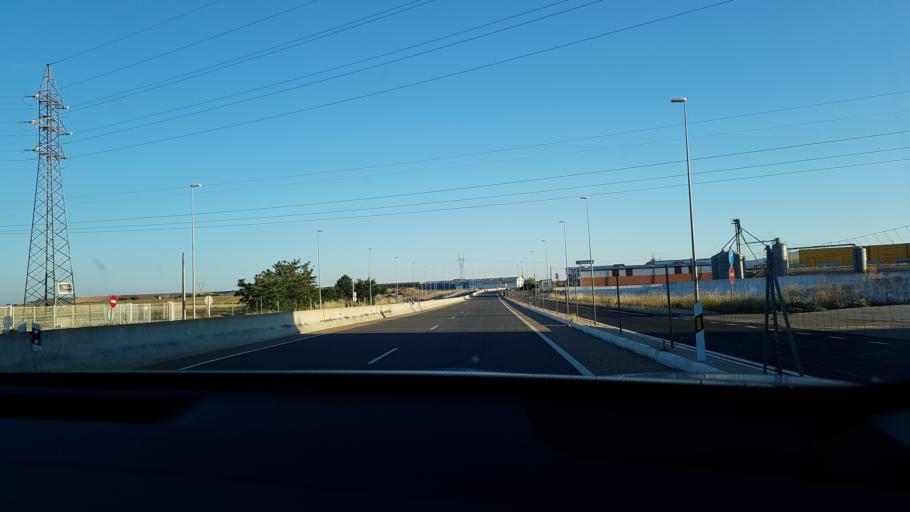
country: ES
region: Castille and Leon
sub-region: Provincia de Zamora
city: Valcabado
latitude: 41.5345
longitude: -5.7615
